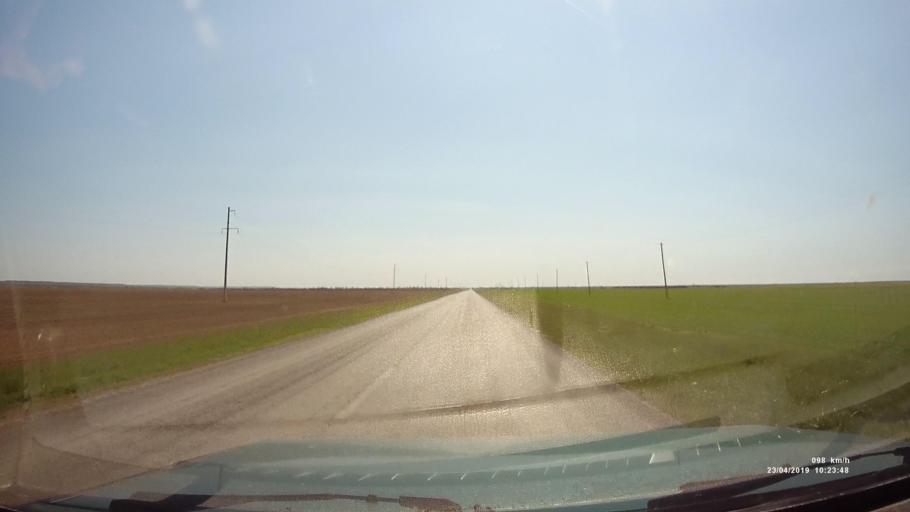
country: RU
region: Rostov
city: Sovetskoye
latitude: 46.6444
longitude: 42.4307
